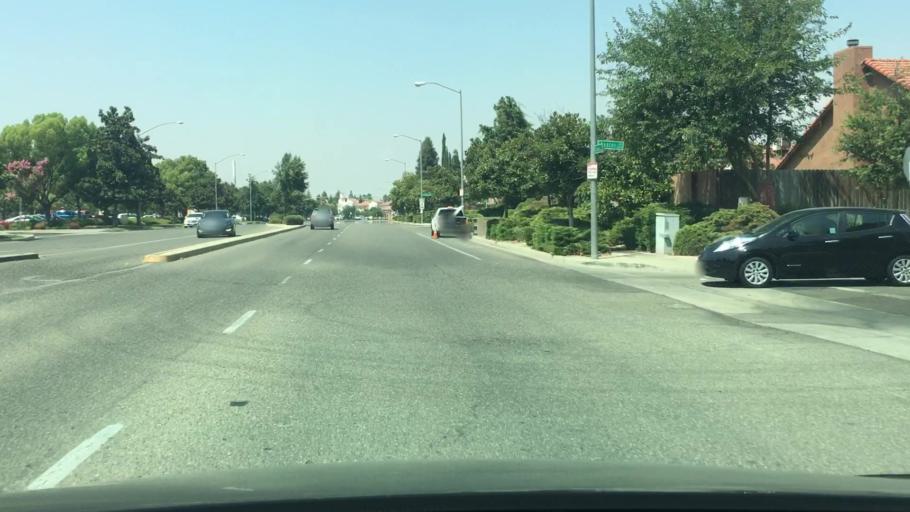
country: US
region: California
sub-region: Fresno County
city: Clovis
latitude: 36.8639
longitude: -119.7567
